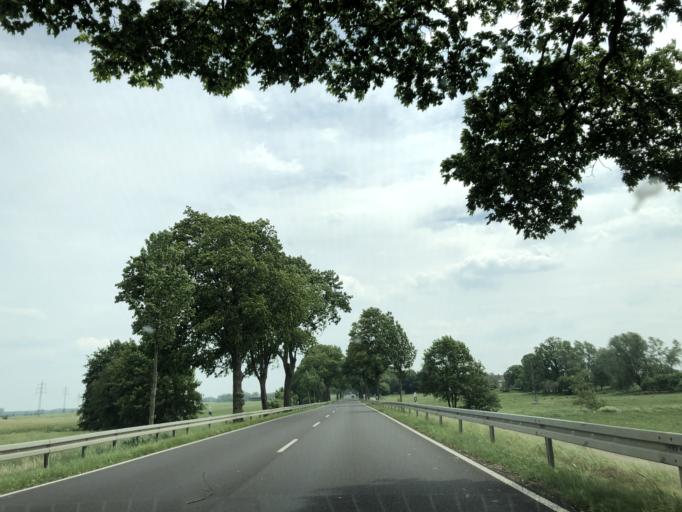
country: DE
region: Brandenburg
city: Kyritz
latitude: 52.9566
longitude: 12.3593
